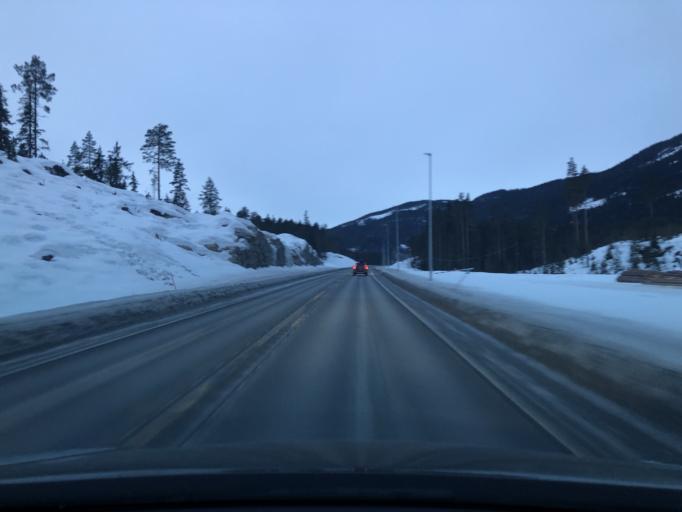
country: NO
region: Oppland
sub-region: Sor-Aurdal
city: Bagn
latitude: 60.8807
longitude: 9.4879
